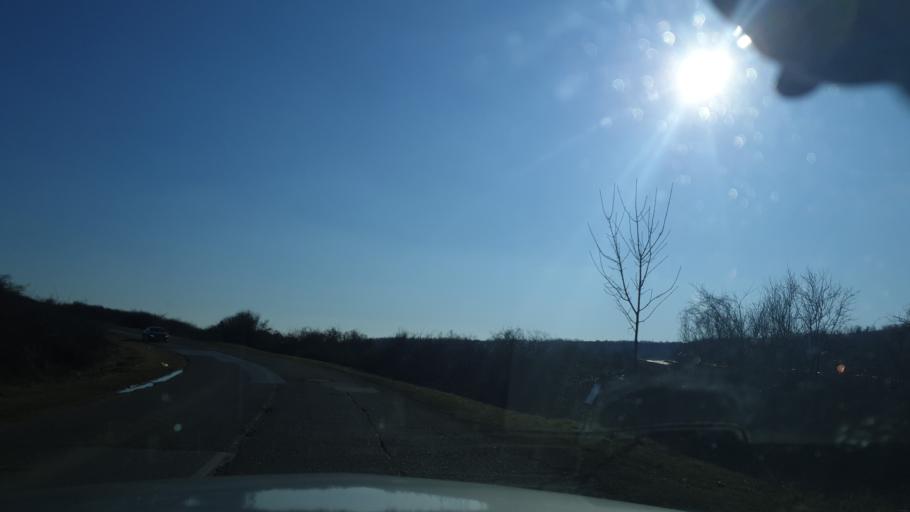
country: RS
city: Vrdnik
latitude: 45.1057
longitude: 19.8010
